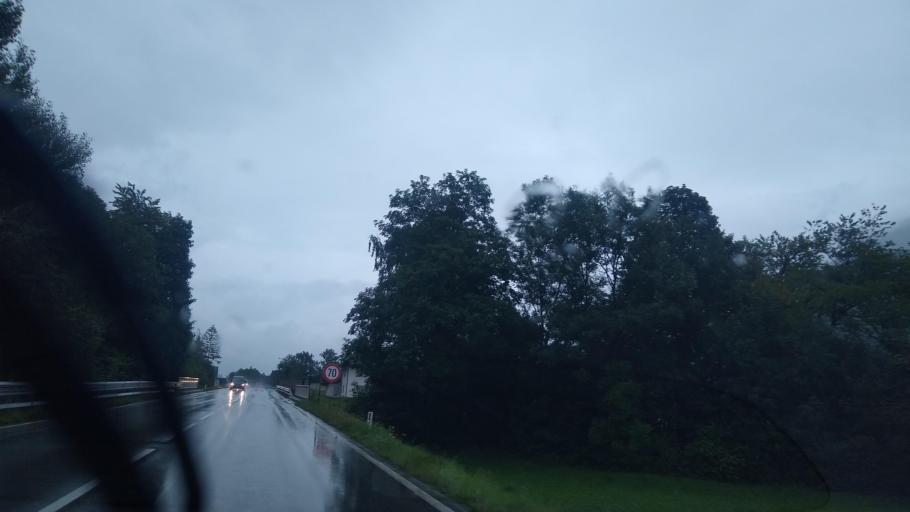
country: AT
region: Tyrol
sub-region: Politischer Bezirk Schwaz
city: Buch bei Jenbach
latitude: 47.3737
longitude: 11.7466
